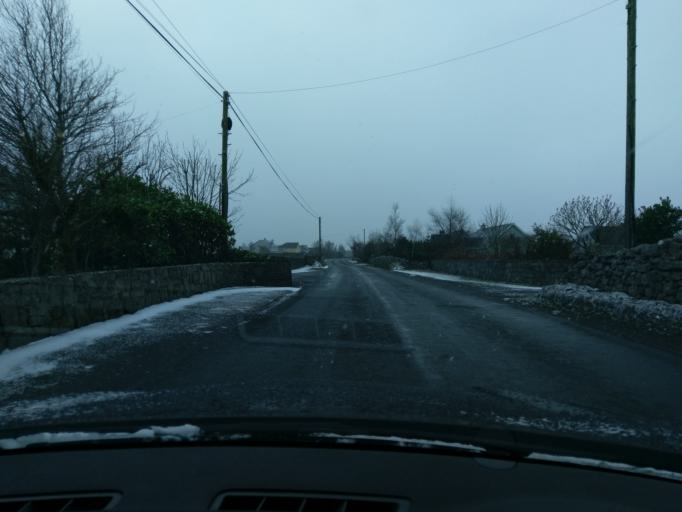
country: IE
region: Connaught
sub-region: County Galway
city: Oranmore
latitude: 53.2547
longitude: -8.8382
